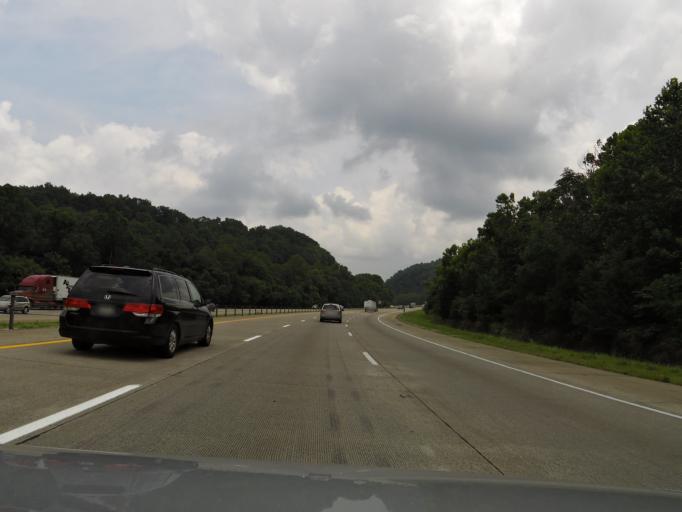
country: US
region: Kentucky
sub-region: Bullitt County
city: Lebanon Junction
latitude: 37.7689
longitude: -85.7901
